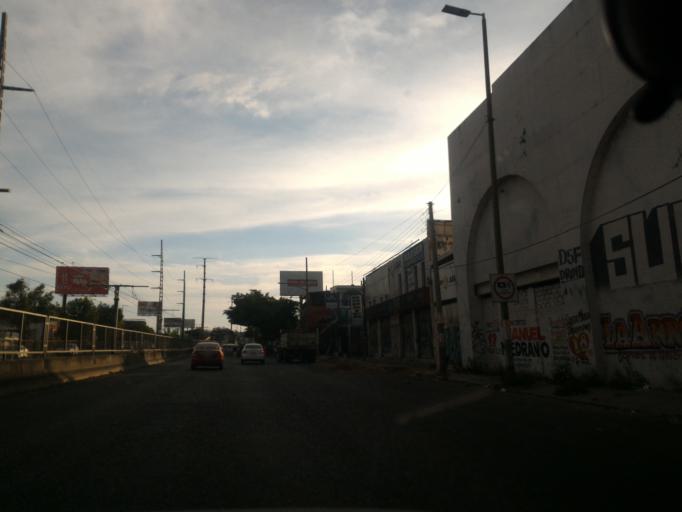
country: MX
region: Jalisco
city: Guadalajara
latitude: 20.6295
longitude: -103.3831
